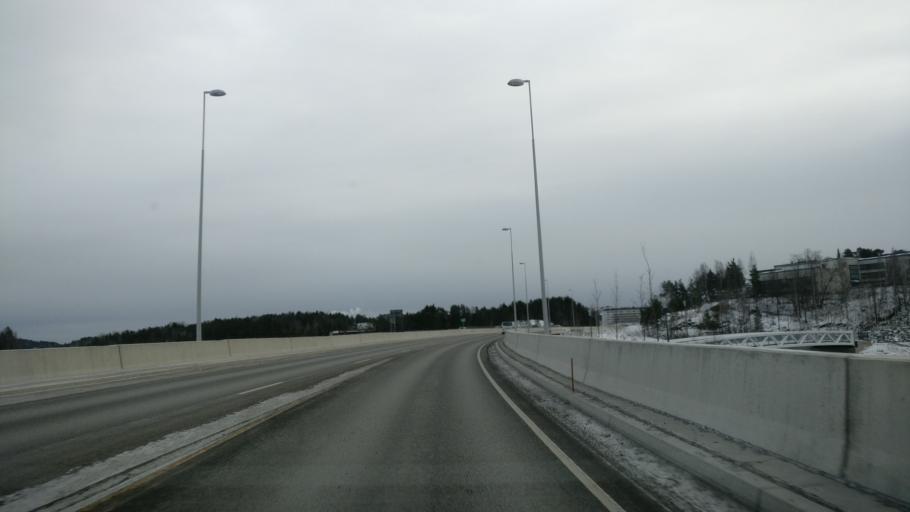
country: FI
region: Southern Savonia
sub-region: Savonlinna
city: Savonlinna
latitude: 61.8752
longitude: 28.8782
